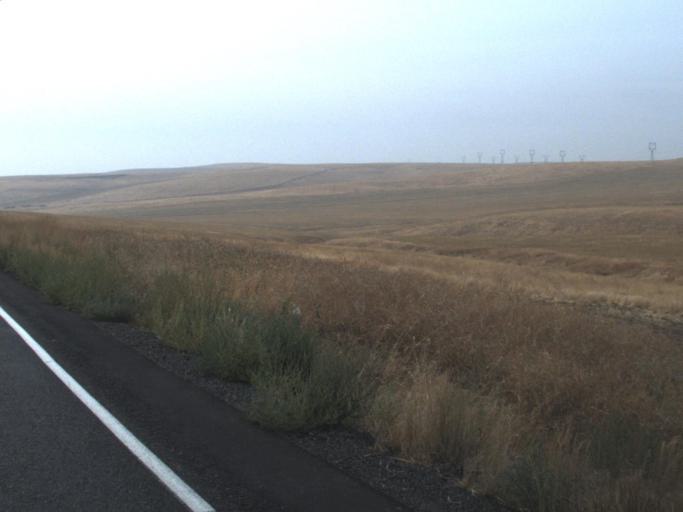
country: US
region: Washington
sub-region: Yakima County
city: Sunnyside
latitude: 46.4616
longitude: -119.9355
